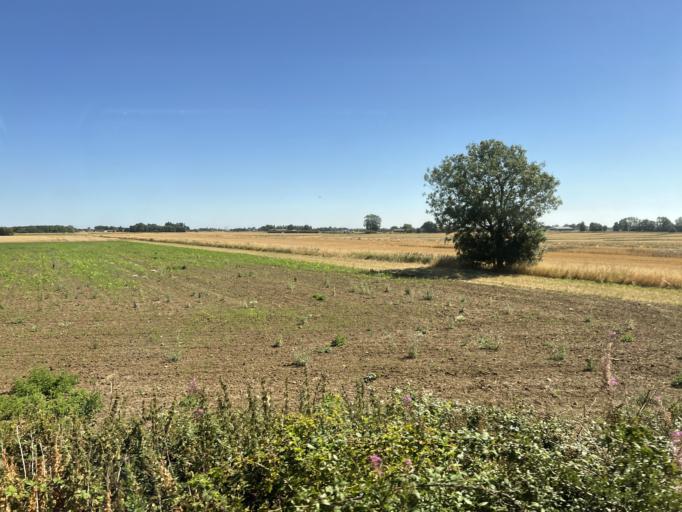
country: GB
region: England
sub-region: Lincolnshire
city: Spilsby
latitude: 53.1359
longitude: 0.1565
